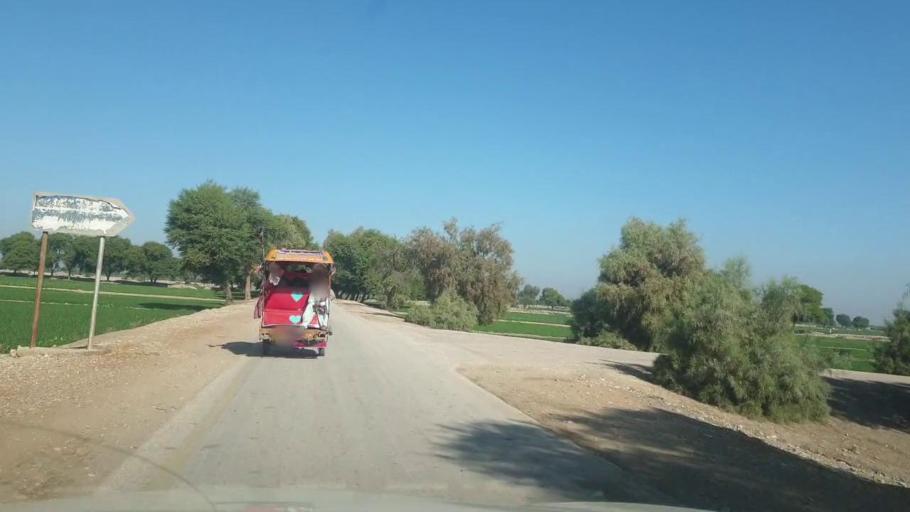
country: PK
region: Sindh
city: Bhan
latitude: 26.5507
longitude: 67.6336
